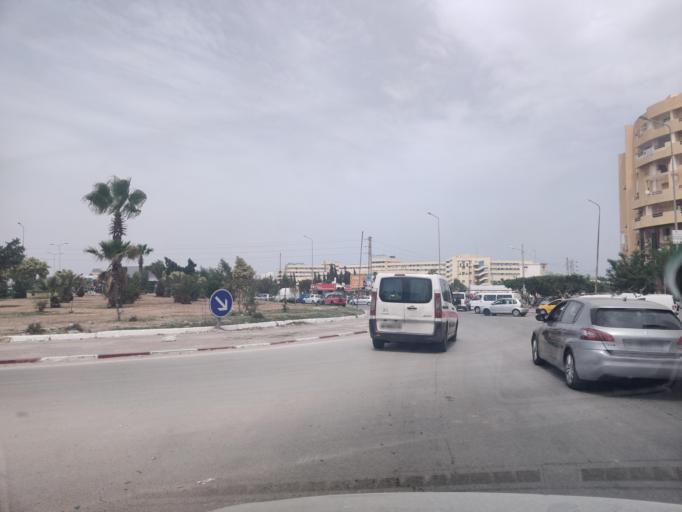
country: TN
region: Susah
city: Hammam Sousse
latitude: 35.8332
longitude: 10.5900
